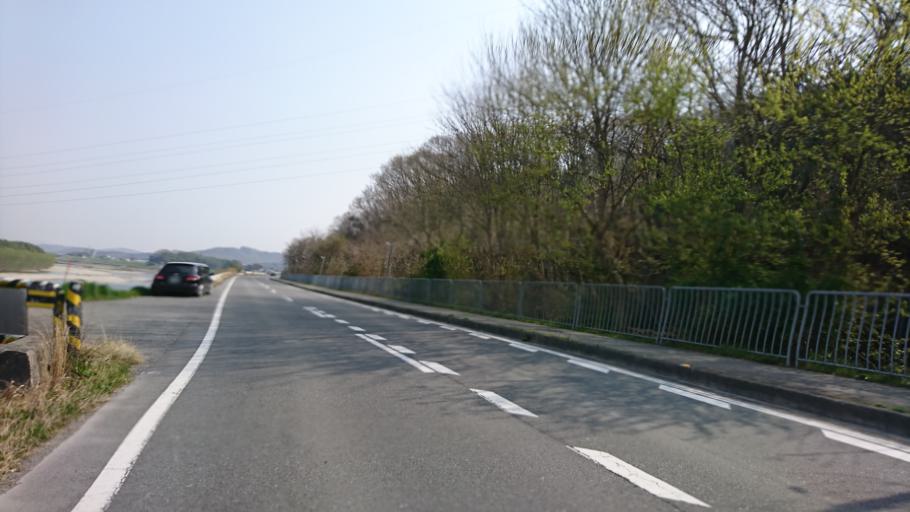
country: JP
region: Hyogo
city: Ono
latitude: 34.8459
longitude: 134.9103
